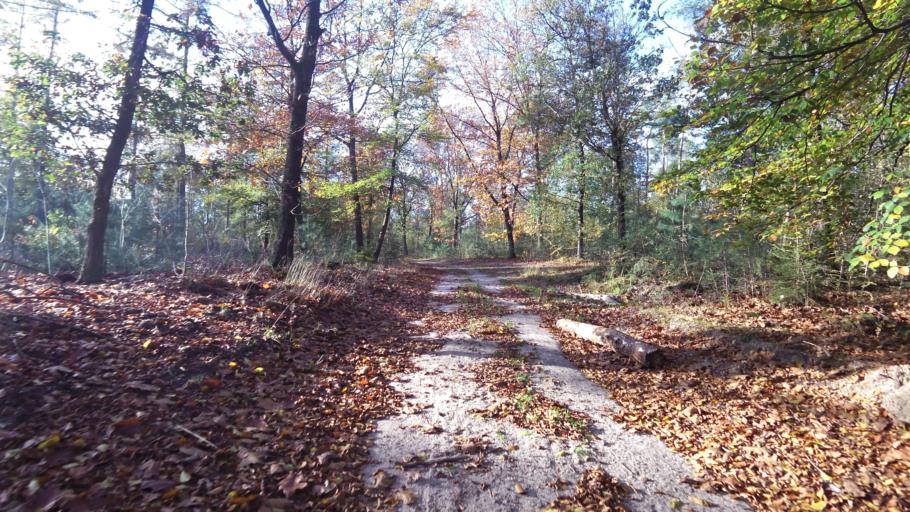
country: NL
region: Gelderland
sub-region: Gemeente Hattem
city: Hattem
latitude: 52.4381
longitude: 6.0382
